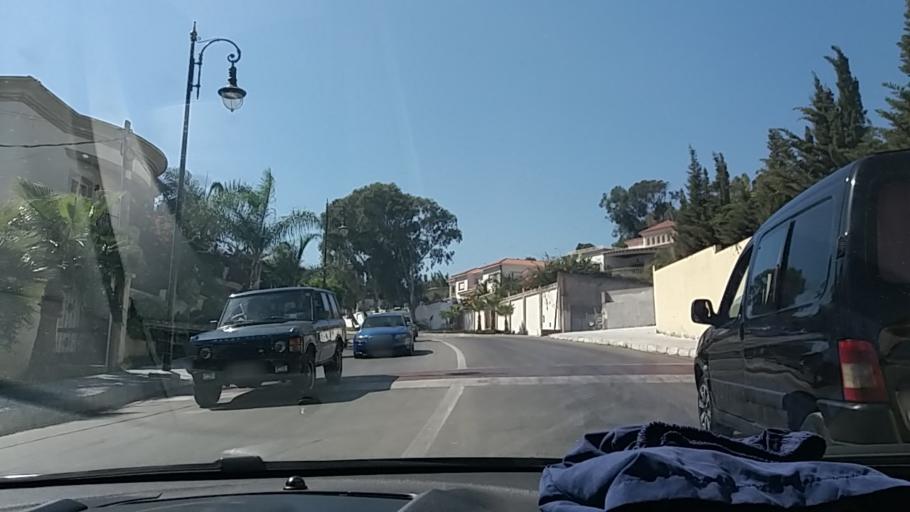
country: MA
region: Tanger-Tetouan
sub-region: Tanger-Assilah
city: Tangier
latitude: 35.7786
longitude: -5.8579
